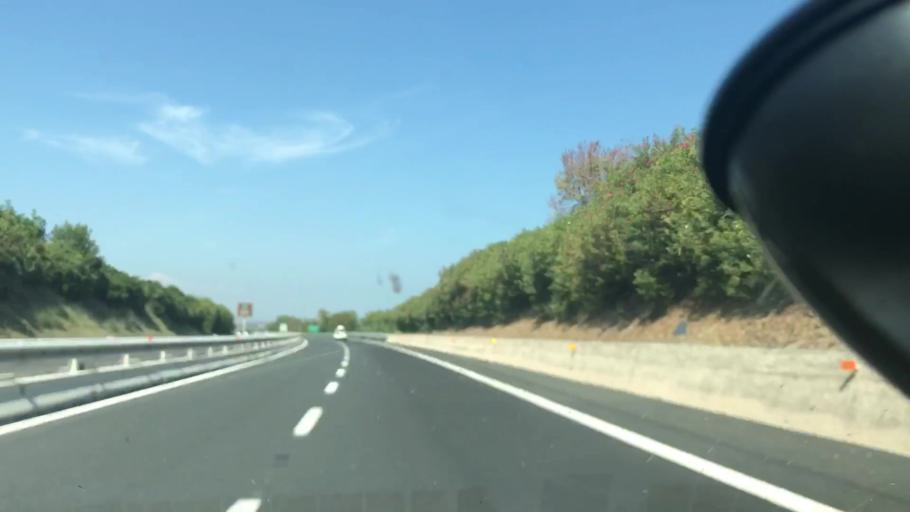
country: IT
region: Abruzzo
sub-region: Provincia di Chieti
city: Vasto
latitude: 42.1327
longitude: 14.6687
